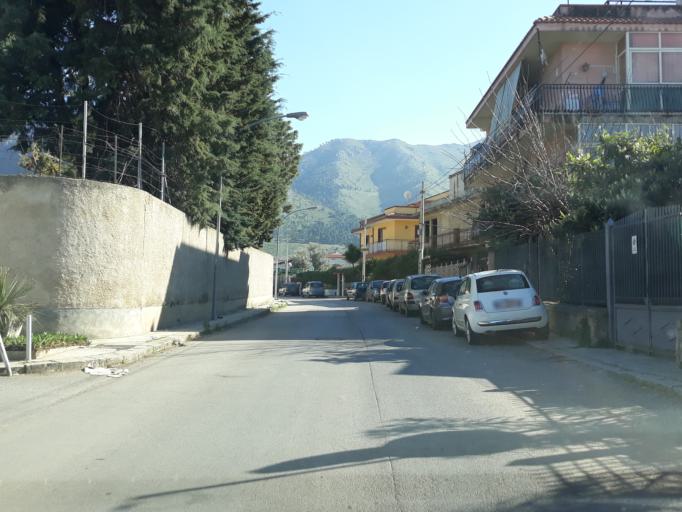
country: IT
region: Sicily
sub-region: Palermo
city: Villa Ciambra
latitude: 38.0856
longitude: 13.3447
